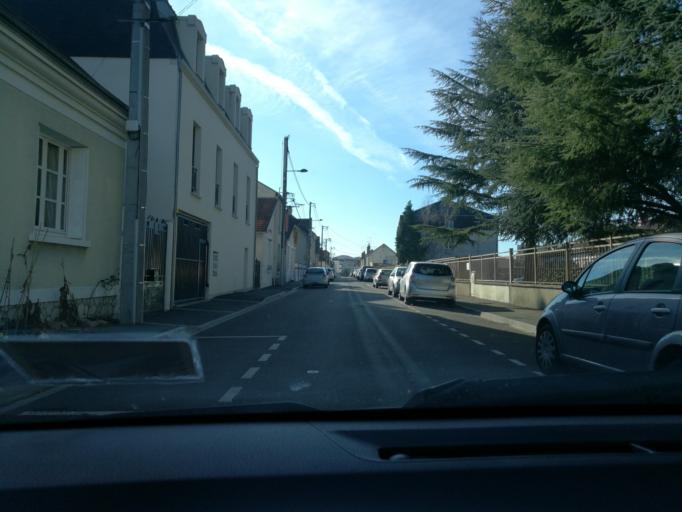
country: FR
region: Centre
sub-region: Departement du Loiret
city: Orleans
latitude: 47.9131
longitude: 1.8901
